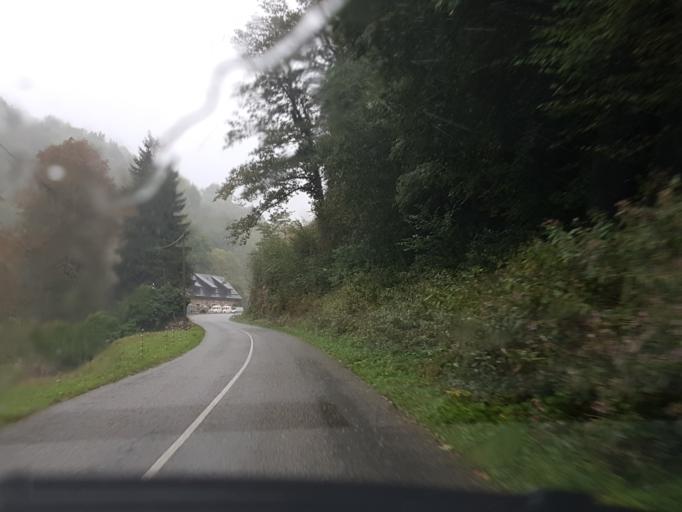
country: FR
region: Midi-Pyrenees
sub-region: Departement de l'Ariege
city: Saint-Girons
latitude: 42.9015
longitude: 1.2994
